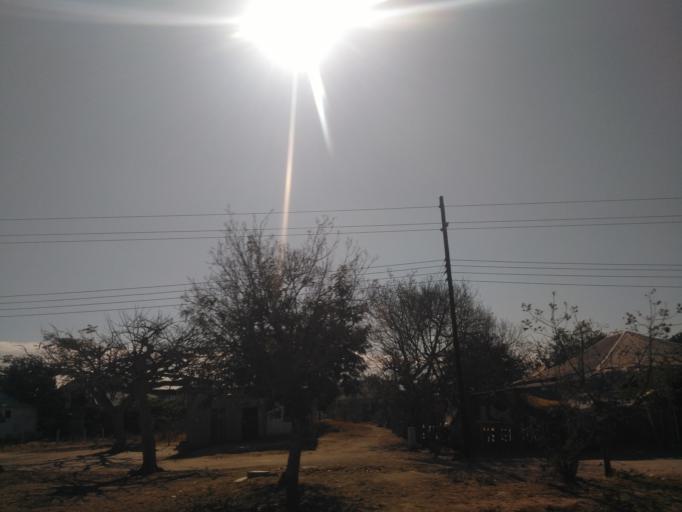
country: TZ
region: Dodoma
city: Dodoma
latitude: -6.1286
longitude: 35.7466
